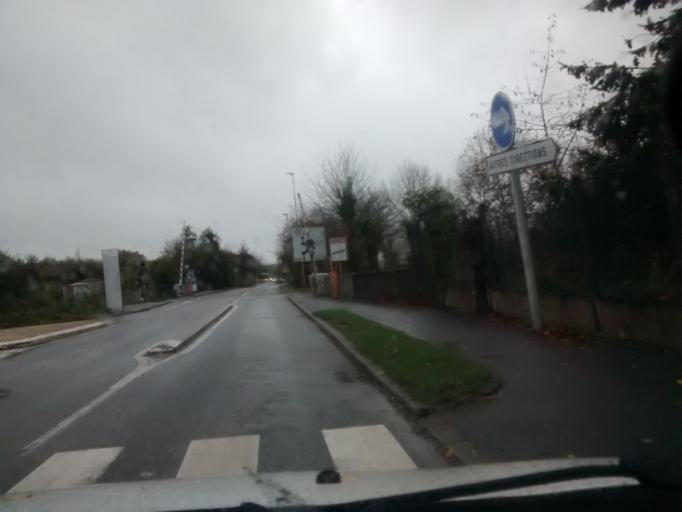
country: FR
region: Brittany
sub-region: Departement d'Ille-et-Vilaine
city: Chantepie
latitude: 48.0854
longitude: -1.6272
